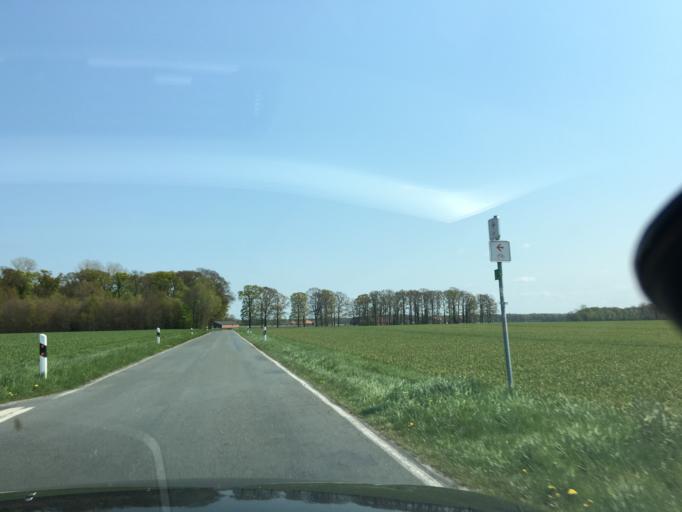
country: DE
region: North Rhine-Westphalia
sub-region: Regierungsbezirk Munster
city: Senden
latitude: 51.8521
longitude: 7.5118
